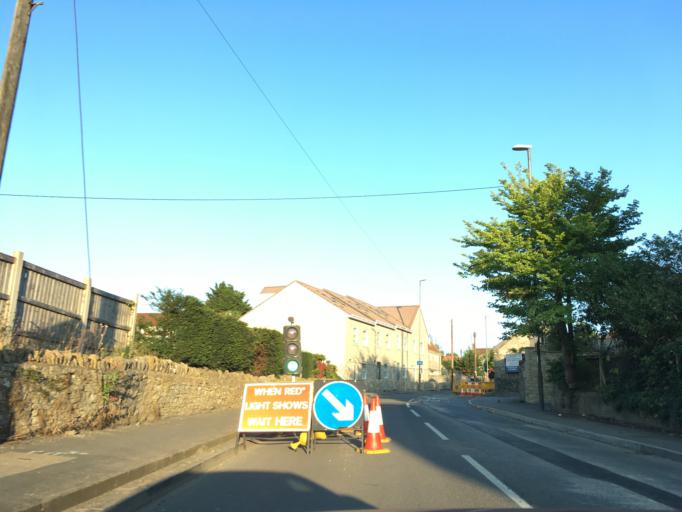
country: GB
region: England
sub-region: Bath and North East Somerset
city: Whitchurch
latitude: 51.4057
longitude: -2.5541
